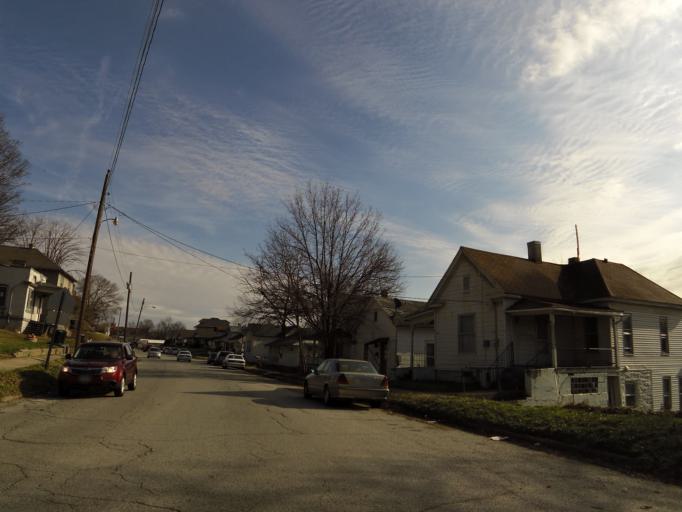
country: US
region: Missouri
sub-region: Marion County
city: Hannibal
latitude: 39.7037
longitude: -91.3839
